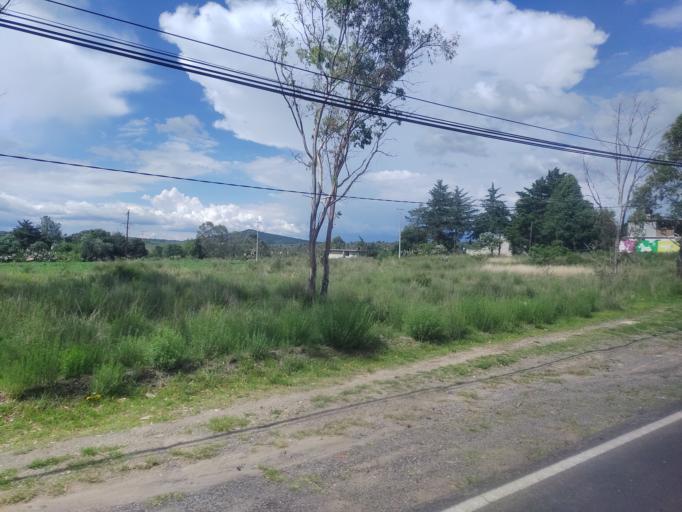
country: MX
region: Mexico
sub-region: Aculco
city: El Colorado
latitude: 20.0932
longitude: -99.7887
